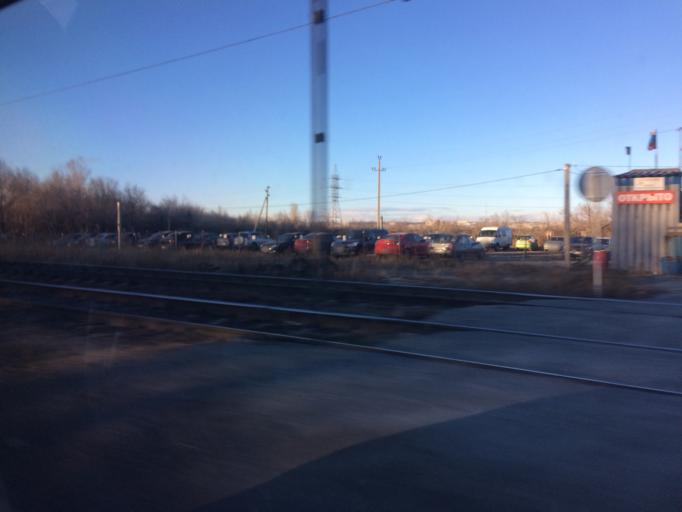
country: RU
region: Chelyabinsk
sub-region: Gorod Magnitogorsk
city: Magnitogorsk
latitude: 53.4059
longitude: 59.0289
